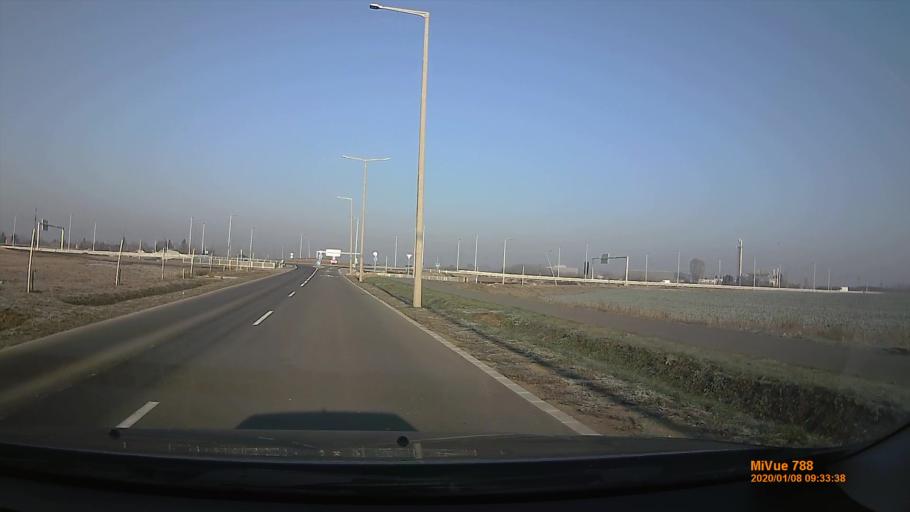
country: HU
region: Bacs-Kiskun
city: Kecskemet
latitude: 46.8695
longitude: 19.6873
